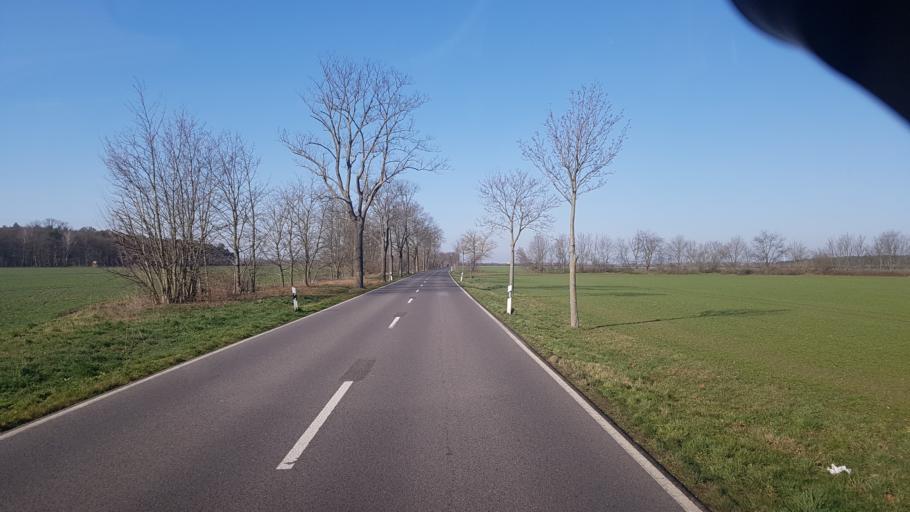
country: DE
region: Brandenburg
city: Luckau
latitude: 51.8497
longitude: 13.7950
